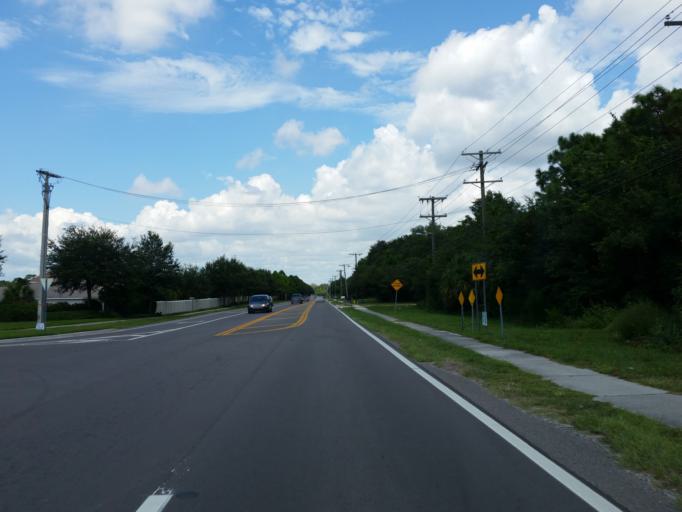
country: US
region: Florida
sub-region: Hillsborough County
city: Riverview
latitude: 27.8327
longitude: -82.3060
